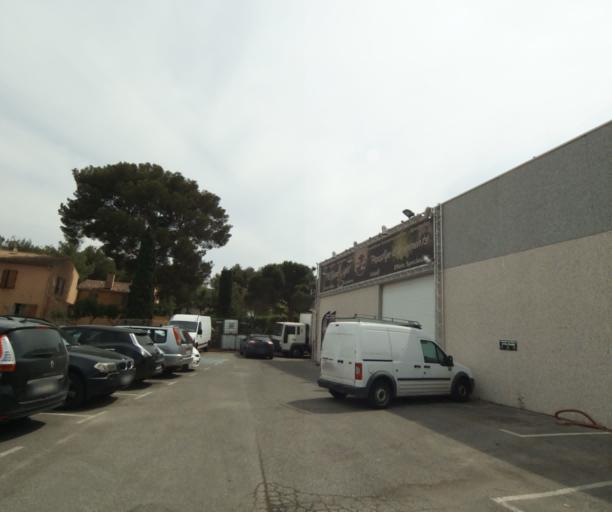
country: FR
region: Provence-Alpes-Cote d'Azur
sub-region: Departement du Var
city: La Garde
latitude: 43.1428
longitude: 6.0236
